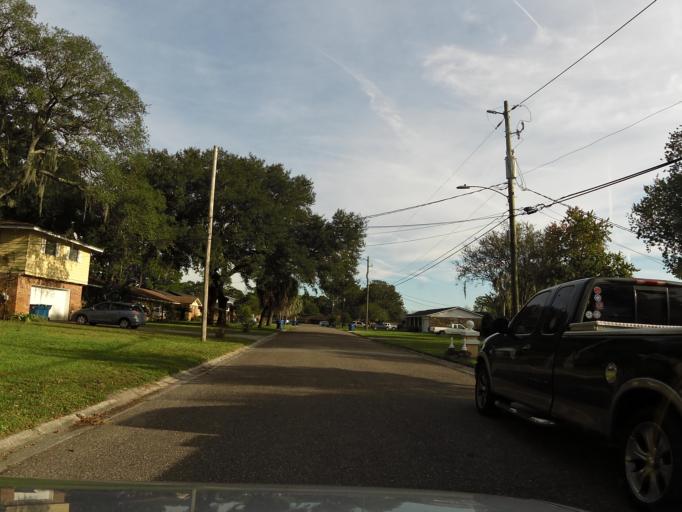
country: US
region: Florida
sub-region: Duval County
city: Jacksonville
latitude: 30.4179
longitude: -81.6688
